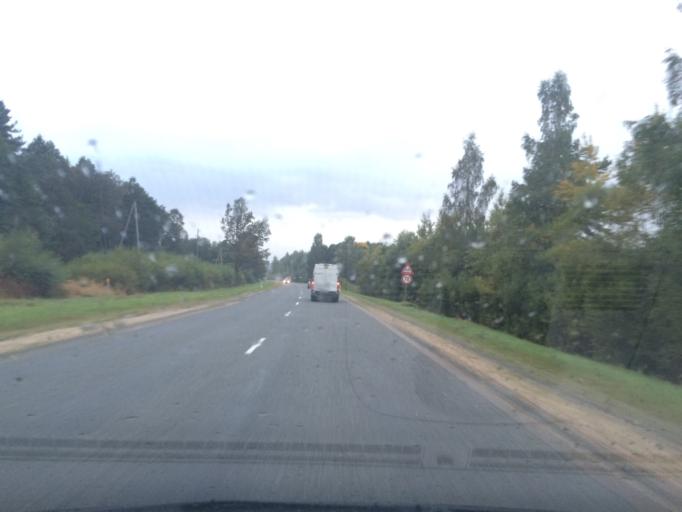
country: LV
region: Plavinu
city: Plavinas
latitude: 56.6212
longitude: 25.7585
